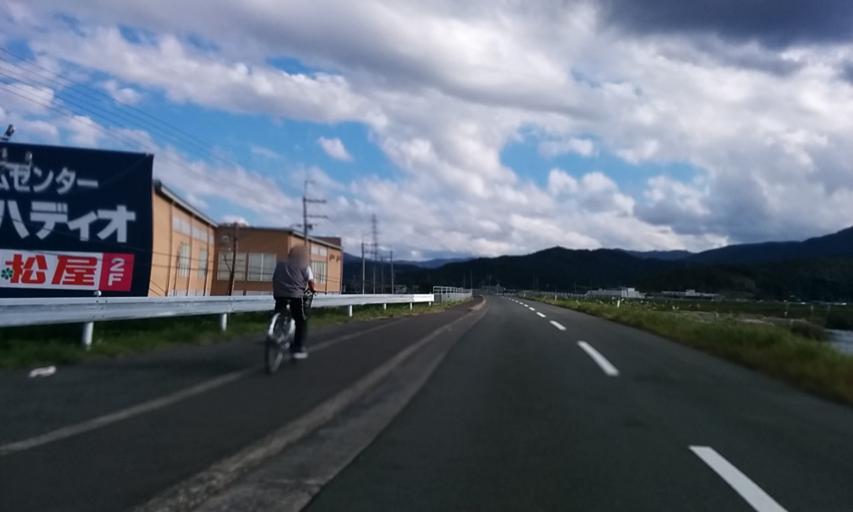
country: JP
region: Fukui
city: Obama
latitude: 35.4942
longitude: 135.7562
